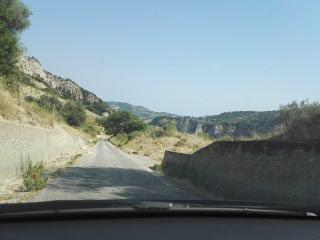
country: IT
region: Calabria
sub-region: Provincia di Reggio Calabria
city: Camini
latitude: 38.4459
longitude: 16.4694
